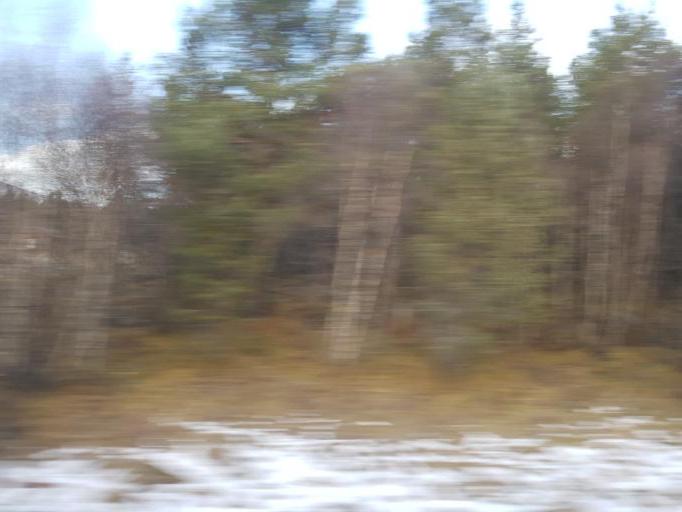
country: NO
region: Sor-Trondelag
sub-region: Oppdal
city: Oppdal
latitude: 62.6584
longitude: 9.8707
